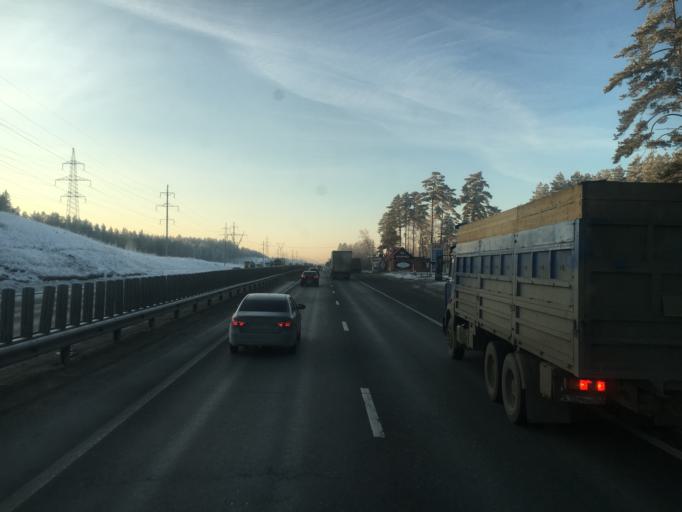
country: RU
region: Samara
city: Pribrezhnyy
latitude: 53.5137
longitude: 49.9053
